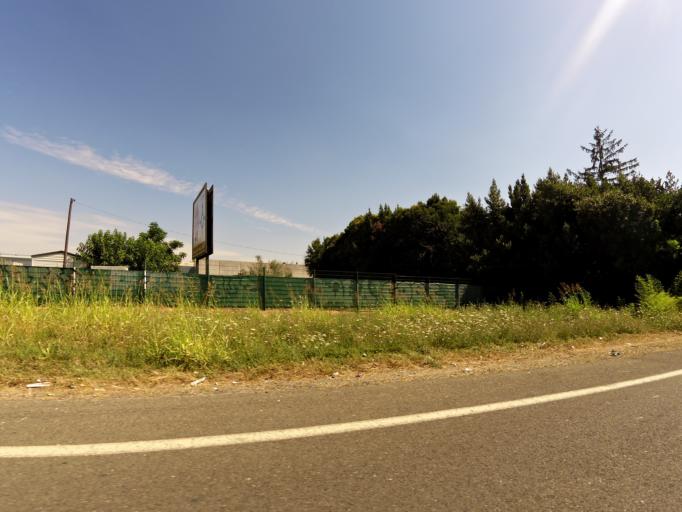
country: FR
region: Languedoc-Roussillon
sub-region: Departement de l'Herault
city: Lunel-Viel
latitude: 43.6789
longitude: 4.1101
